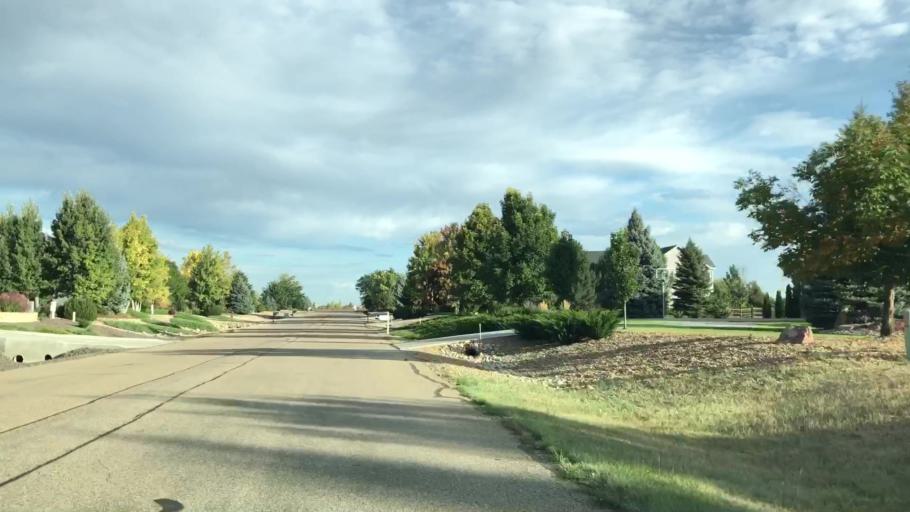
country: US
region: Colorado
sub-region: Weld County
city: Windsor
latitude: 40.4413
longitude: -104.9518
